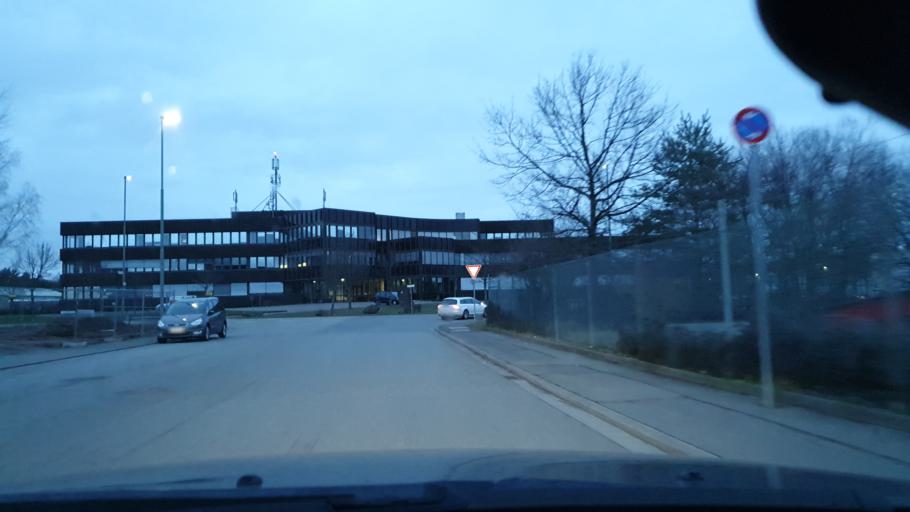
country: DE
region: Rheinland-Pfalz
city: Rodenbach
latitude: 49.4384
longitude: 7.6658
